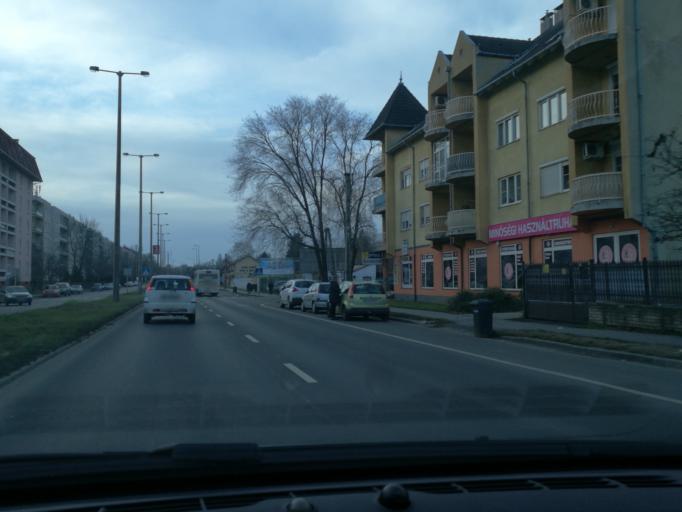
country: HU
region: Szabolcs-Szatmar-Bereg
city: Nyiregyhaza
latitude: 47.9485
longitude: 21.7264
